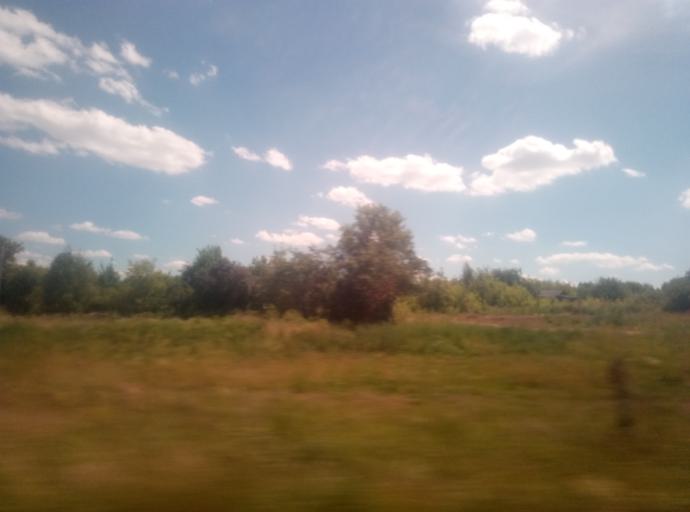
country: RU
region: Tula
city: Kireyevsk
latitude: 53.9371
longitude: 37.9464
